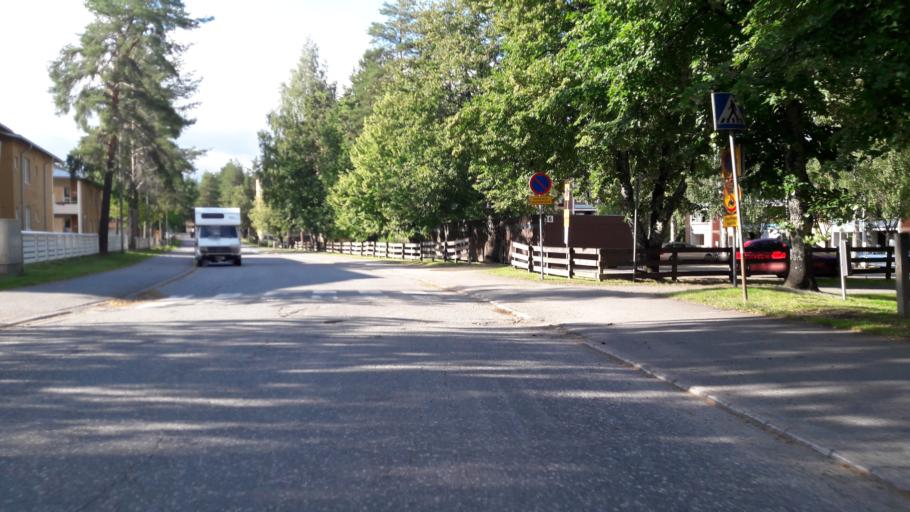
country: FI
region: North Karelia
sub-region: Joensuu
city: Joensuu
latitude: 62.6039
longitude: 29.8000
